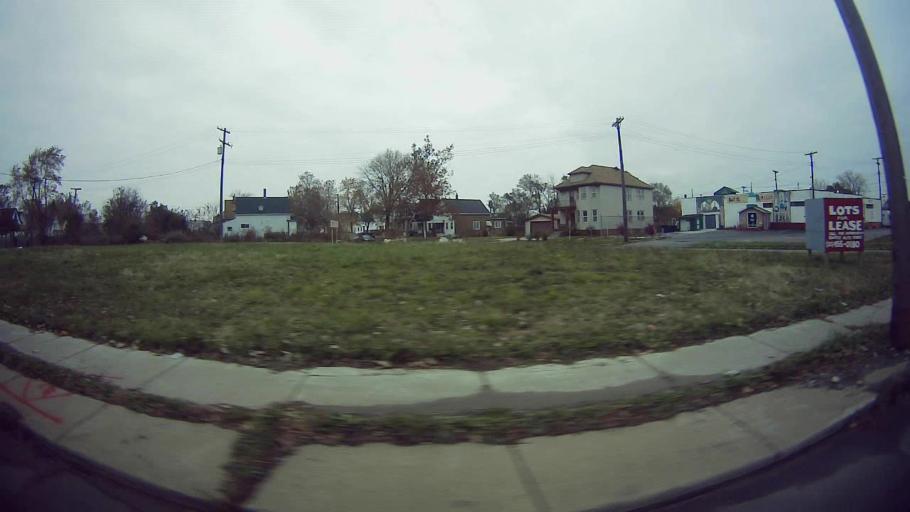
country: US
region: Michigan
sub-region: Wayne County
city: Hamtramck
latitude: 42.3870
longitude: -83.0403
